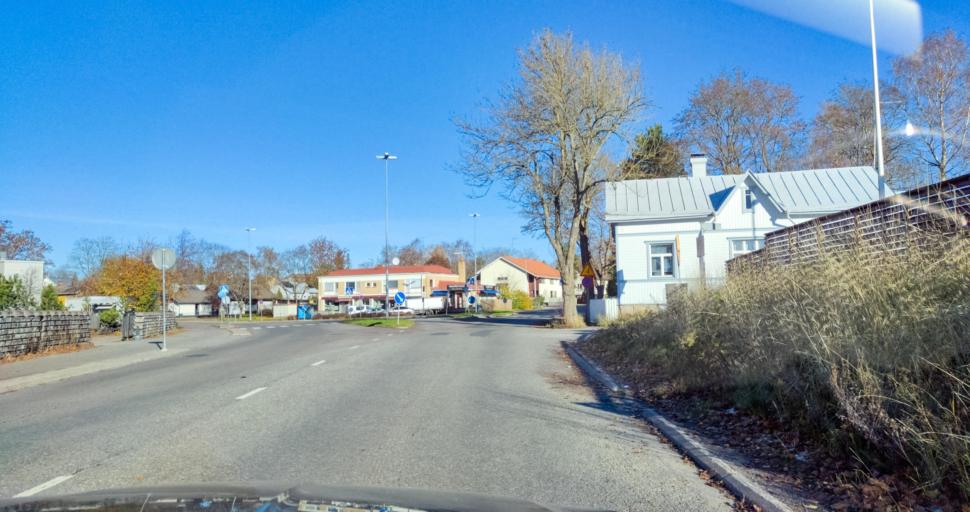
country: FI
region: Varsinais-Suomi
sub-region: Turku
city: Turku
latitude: 60.4344
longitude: 22.2591
